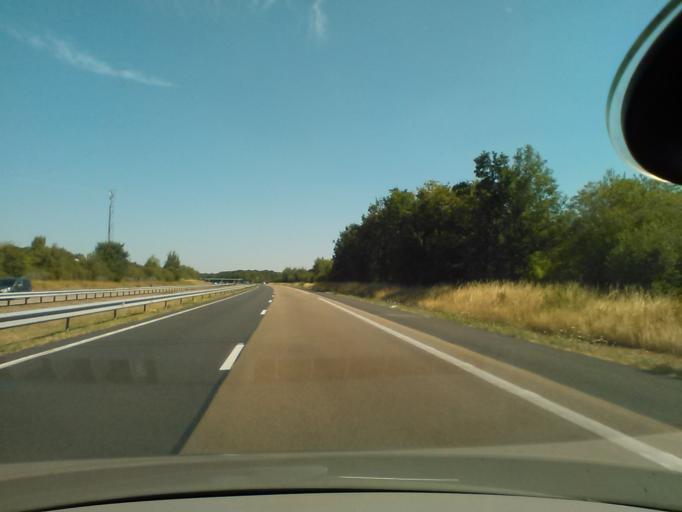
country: FR
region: Bourgogne
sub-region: Departement de l'Yonne
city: Cheroy
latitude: 48.1174
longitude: 2.9805
